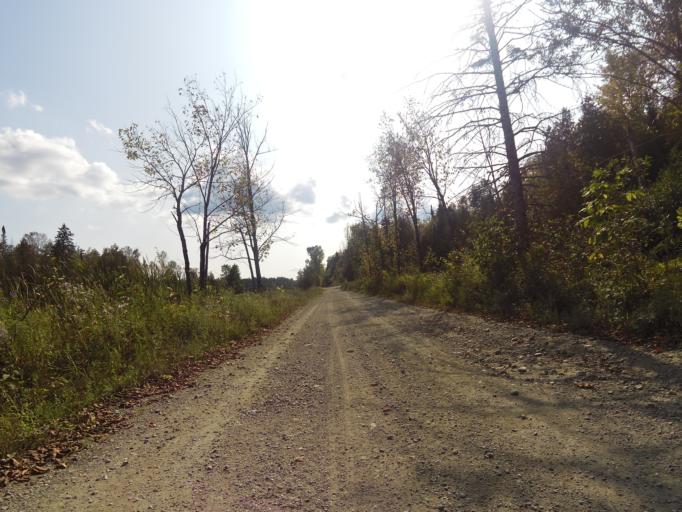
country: CA
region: Ontario
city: Renfrew
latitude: 45.1259
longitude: -76.6884
